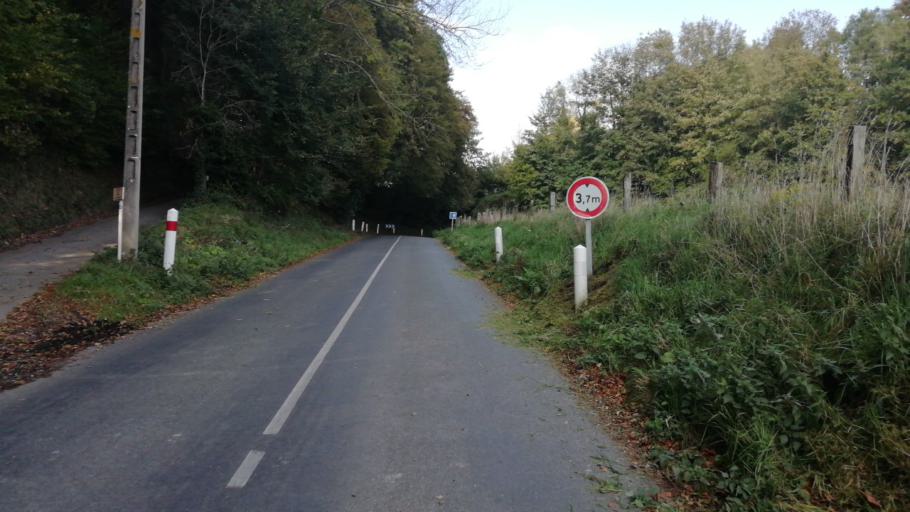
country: FR
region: Haute-Normandie
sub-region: Departement de la Seine-Maritime
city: Rolleville
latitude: 49.5969
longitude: 0.2118
